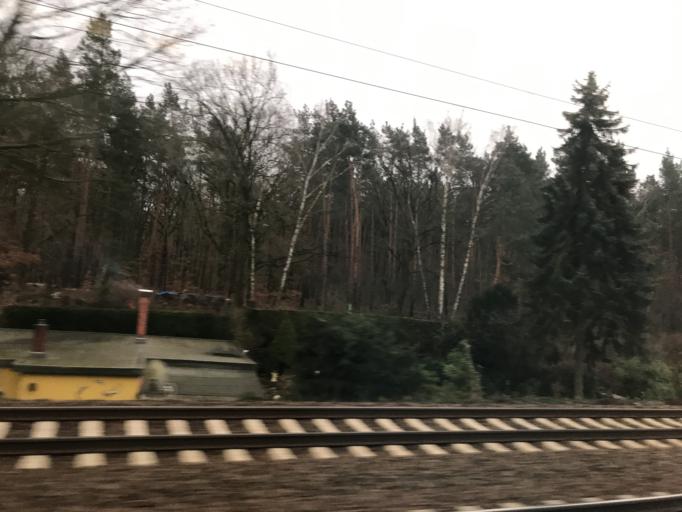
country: DE
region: Berlin
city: Grunewald
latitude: 52.4719
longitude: 13.2411
